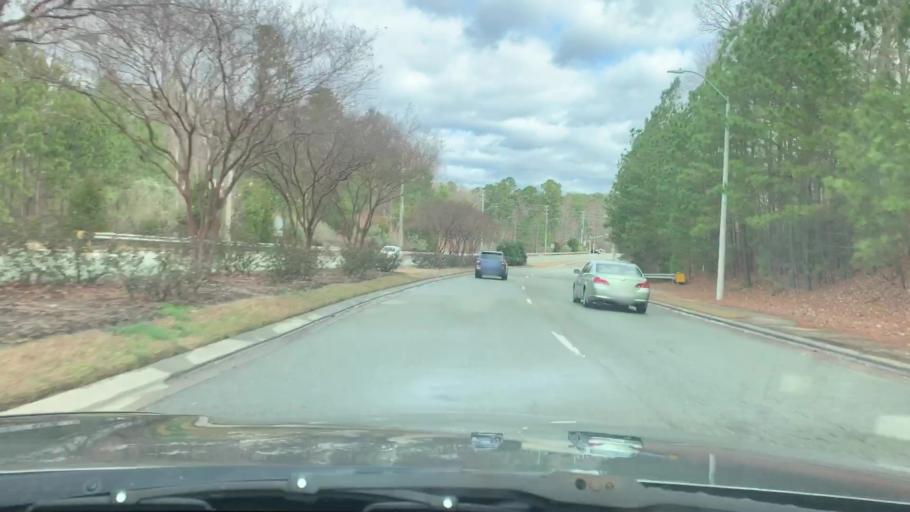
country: US
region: North Carolina
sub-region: Wake County
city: Cary
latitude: 35.8077
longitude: -78.7826
